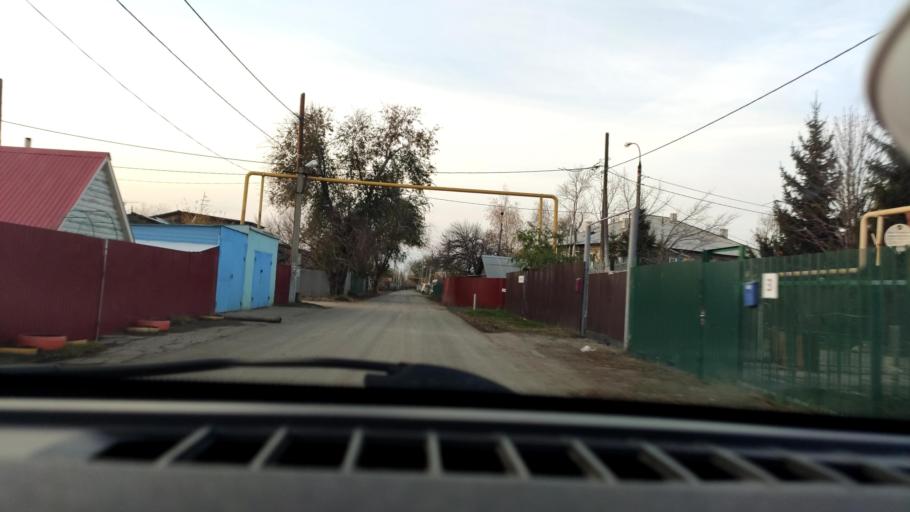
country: RU
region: Samara
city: Samara
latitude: 53.1393
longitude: 50.1355
